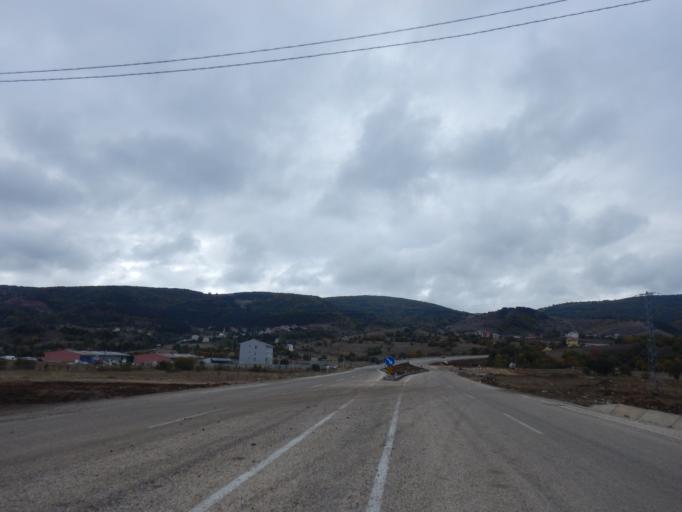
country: TR
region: Ordu
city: Mesudiye
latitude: 40.4459
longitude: 37.7785
